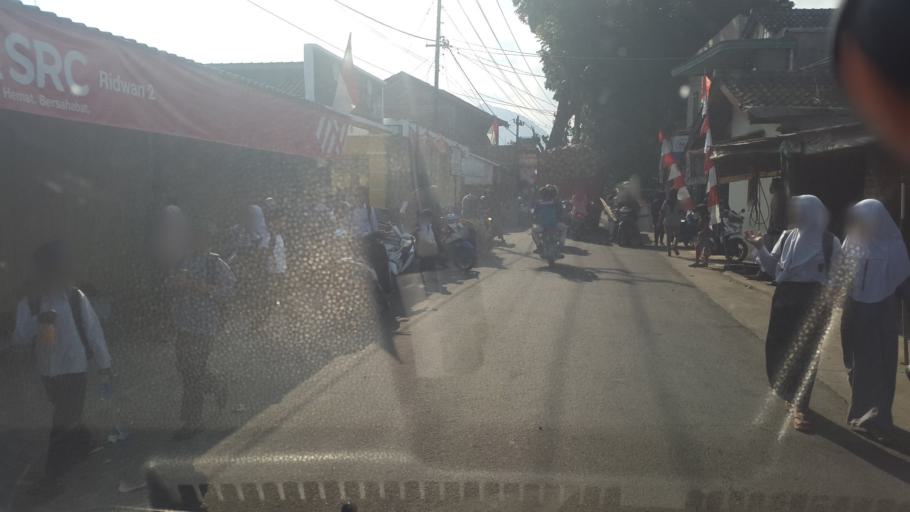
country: ID
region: West Java
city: Cicurug
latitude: -6.8263
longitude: 106.7347
